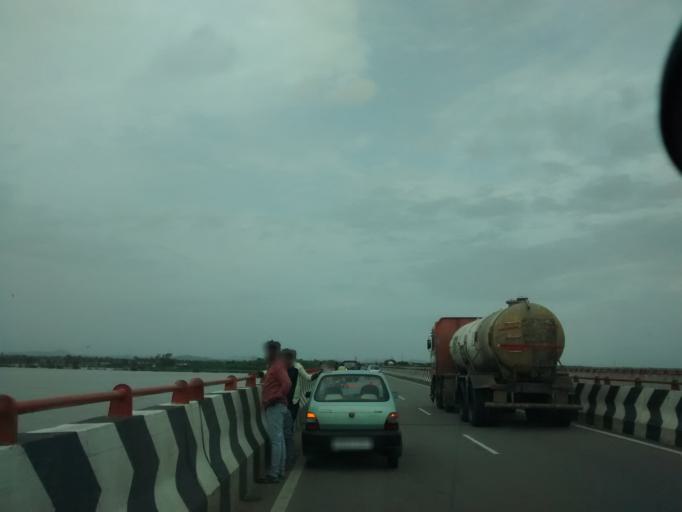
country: IN
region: Telangana
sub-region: Mahbubnagar
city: Gadwal
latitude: 16.1617
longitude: 77.9343
